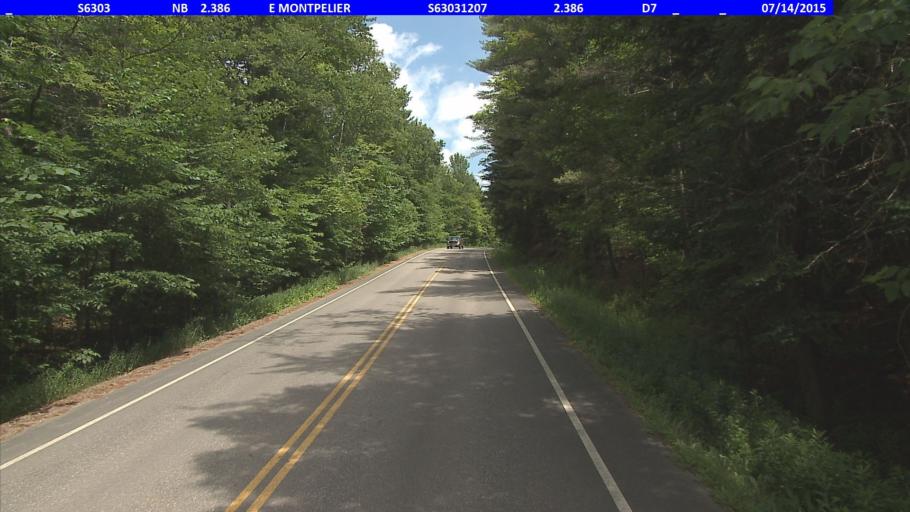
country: US
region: Vermont
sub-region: Washington County
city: Montpelier
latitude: 44.3024
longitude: -72.5332
